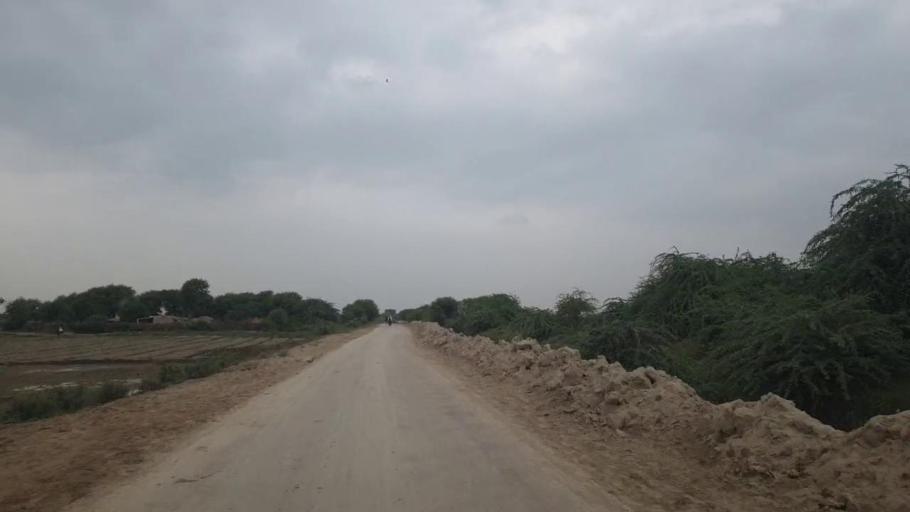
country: PK
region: Sindh
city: Badin
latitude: 24.6445
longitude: 68.6808
